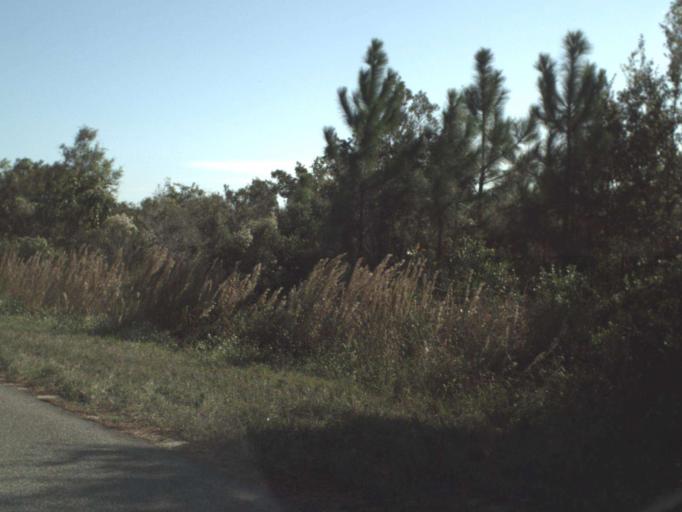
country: US
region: Florida
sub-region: Franklin County
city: Apalachicola
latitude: 29.7216
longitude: -85.0708
